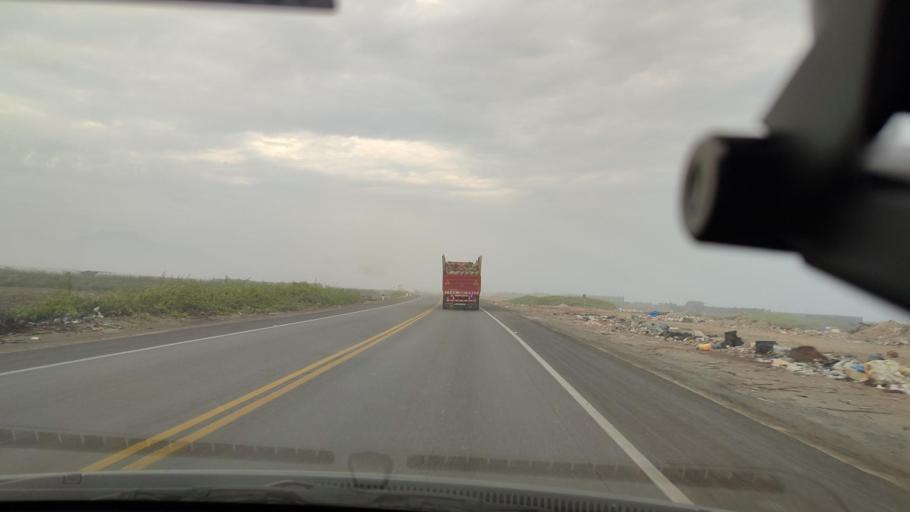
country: PE
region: La Libertad
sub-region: Provincia de Trujillo
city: Huanchaco
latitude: -8.1114
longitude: -79.0948
